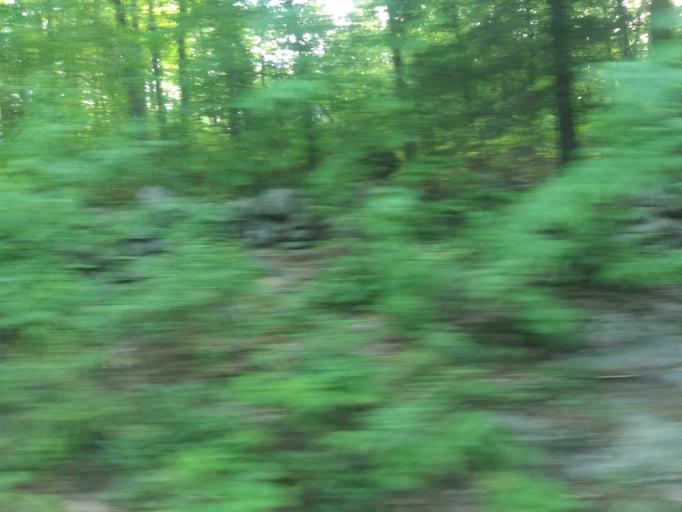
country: US
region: Massachusetts
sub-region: Franklin County
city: Buckland
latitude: 42.5702
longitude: -72.7674
